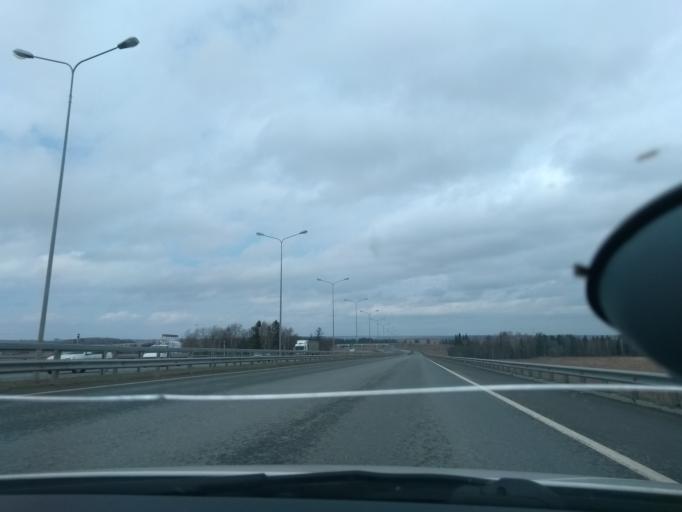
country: RU
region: Perm
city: Zvezdnyy
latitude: 57.7739
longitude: 56.3382
